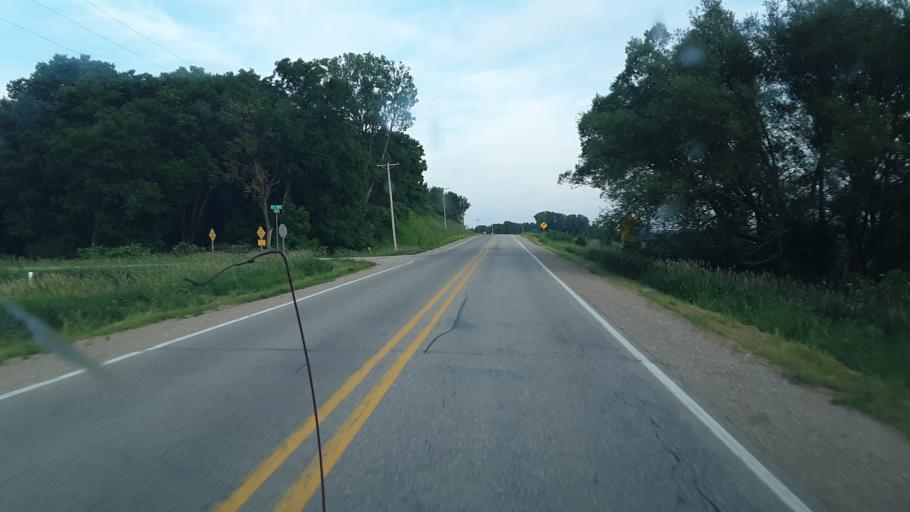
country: US
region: Iowa
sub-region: Tama County
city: Tama
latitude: 41.9576
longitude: -92.4264
